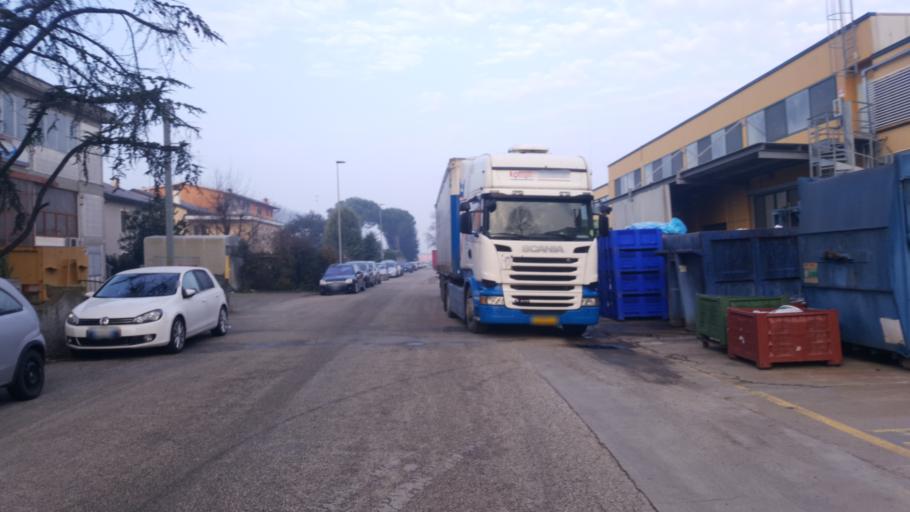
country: IT
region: Emilia-Romagna
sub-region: Provincia di Ravenna
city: Bagnacavallo
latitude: 44.4095
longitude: 11.9932
